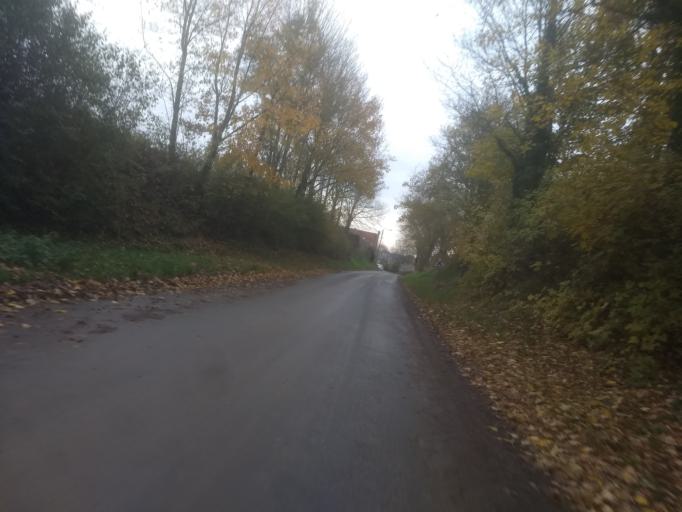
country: FR
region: Nord-Pas-de-Calais
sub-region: Departement du Pas-de-Calais
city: Dainville
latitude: 50.2494
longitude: 2.7216
